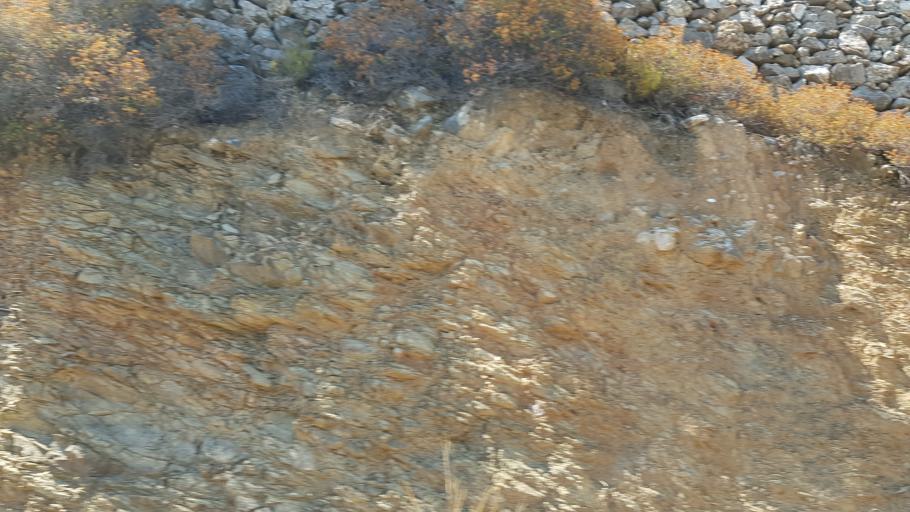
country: TR
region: Mugla
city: Karaova
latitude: 37.0169
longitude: 27.7385
